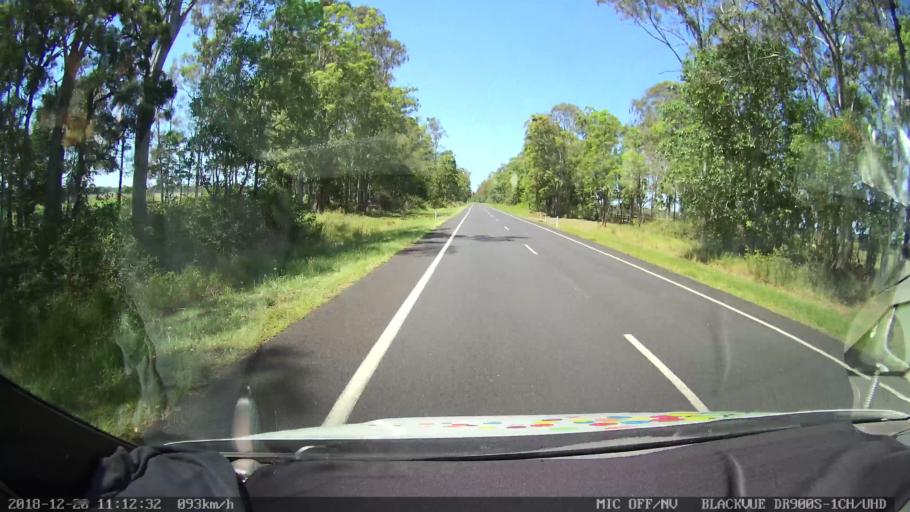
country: AU
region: New South Wales
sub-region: Richmond Valley
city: Casino
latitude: -28.9754
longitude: 153.0107
